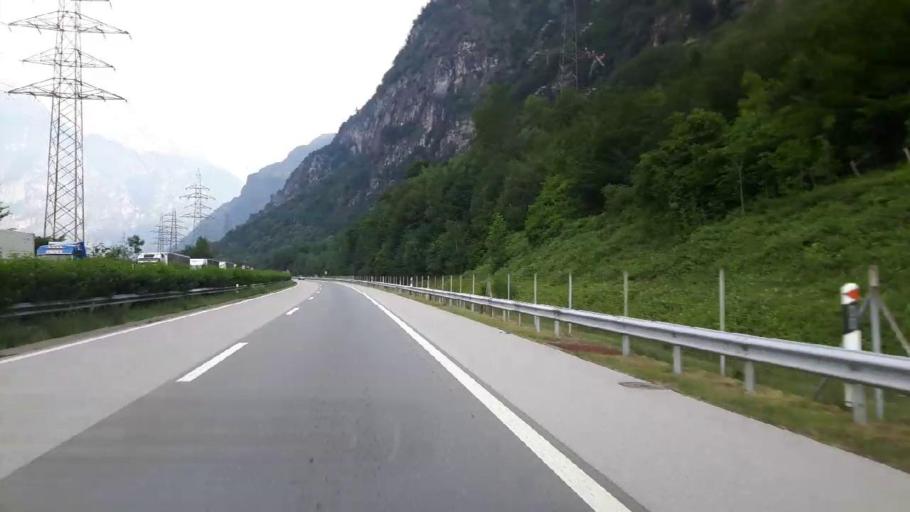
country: CH
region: Ticino
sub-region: Leventina District
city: Bodio
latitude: 46.3852
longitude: 8.8912
